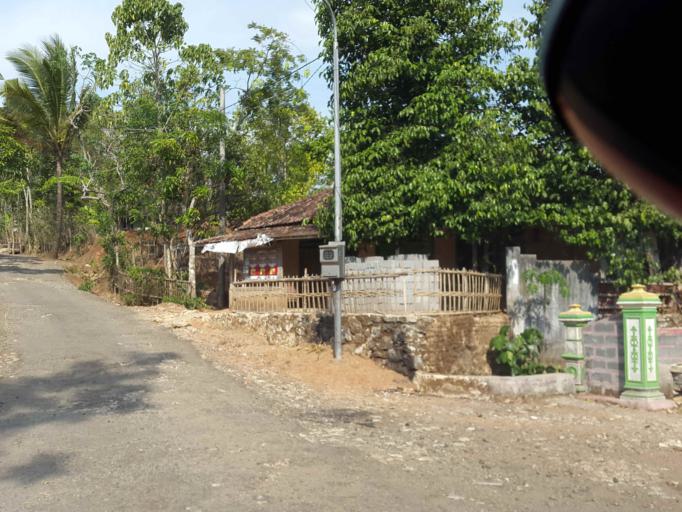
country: ID
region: East Java
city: Krajan
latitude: -8.1002
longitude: 111.0248
